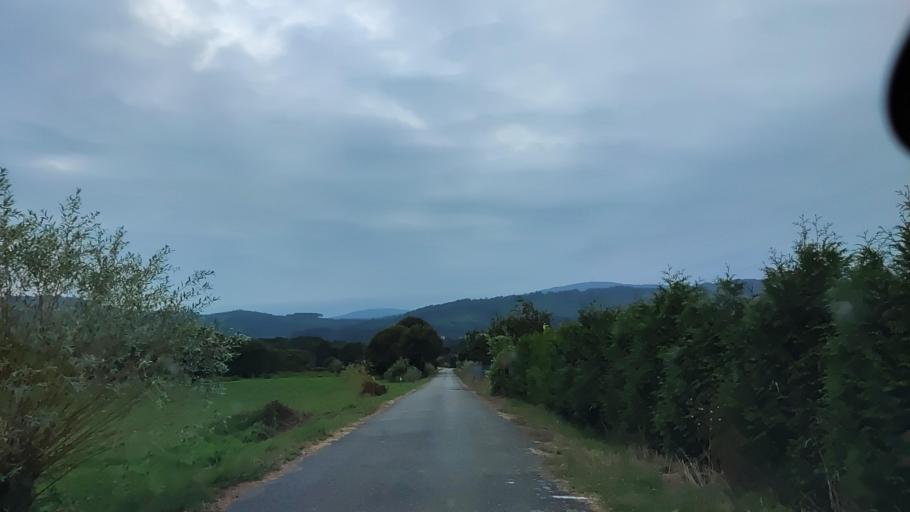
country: ES
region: Galicia
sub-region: Provincia da Coruna
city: Rois
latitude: 42.7141
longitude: -8.7032
